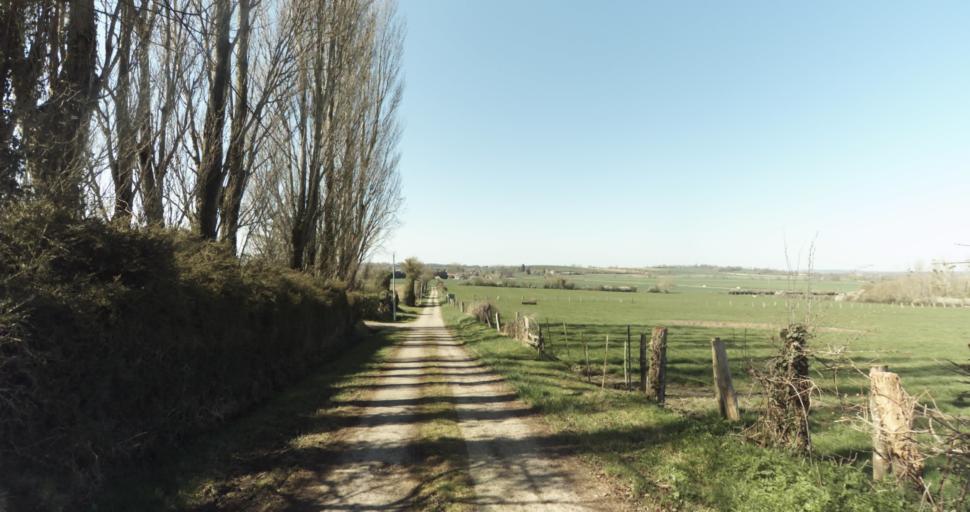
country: FR
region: Lower Normandy
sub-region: Departement du Calvados
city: Saint-Pierre-sur-Dives
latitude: 49.0150
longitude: 0.0342
